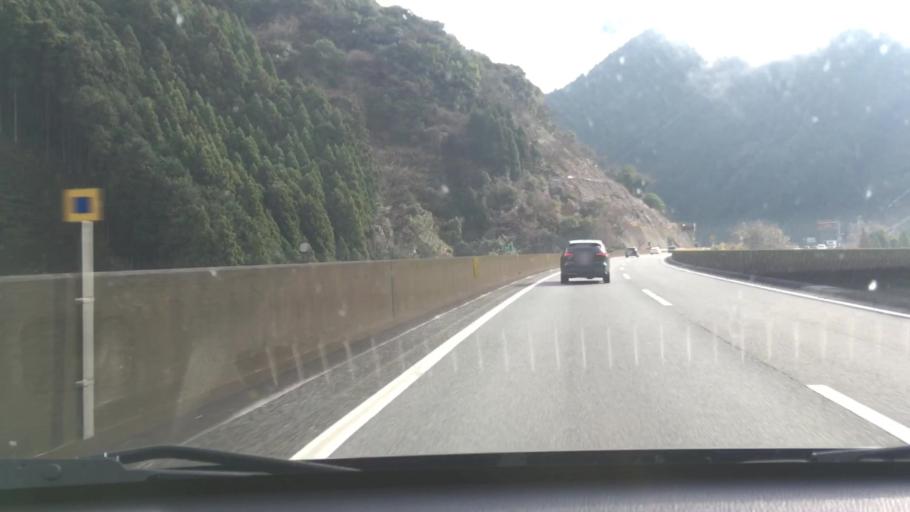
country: JP
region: Kumamoto
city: Yatsushiro
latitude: 32.4288
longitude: 130.7024
